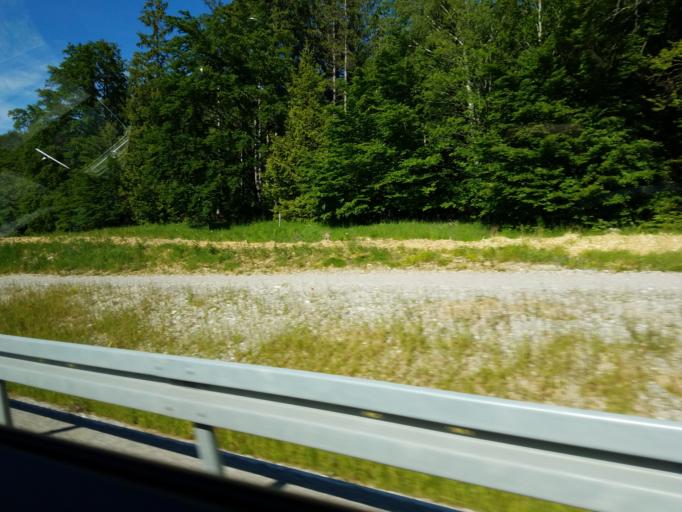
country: DE
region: Bavaria
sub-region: Upper Bavaria
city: Pocking
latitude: 48.0031
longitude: 11.2931
